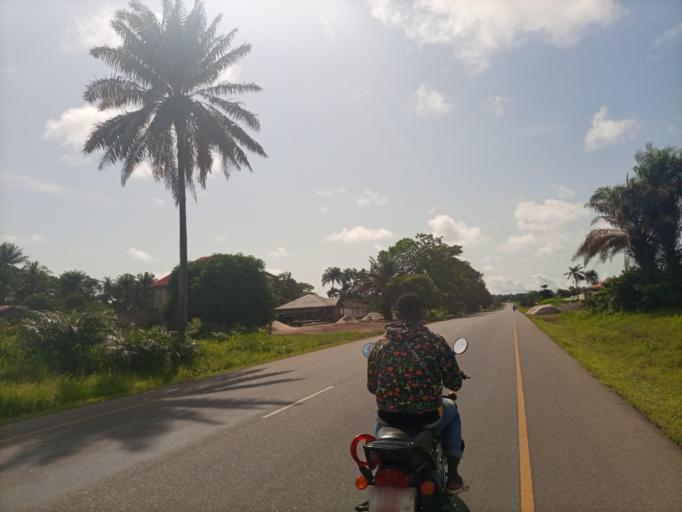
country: SL
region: Northern Province
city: Sawkta
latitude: 8.6303
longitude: -13.1817
